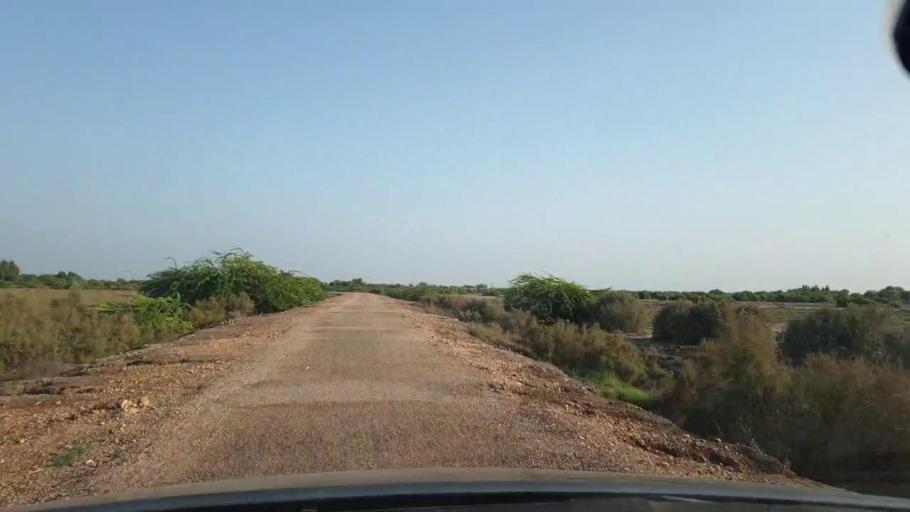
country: PK
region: Sindh
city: Naukot
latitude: 24.8168
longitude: 69.2006
